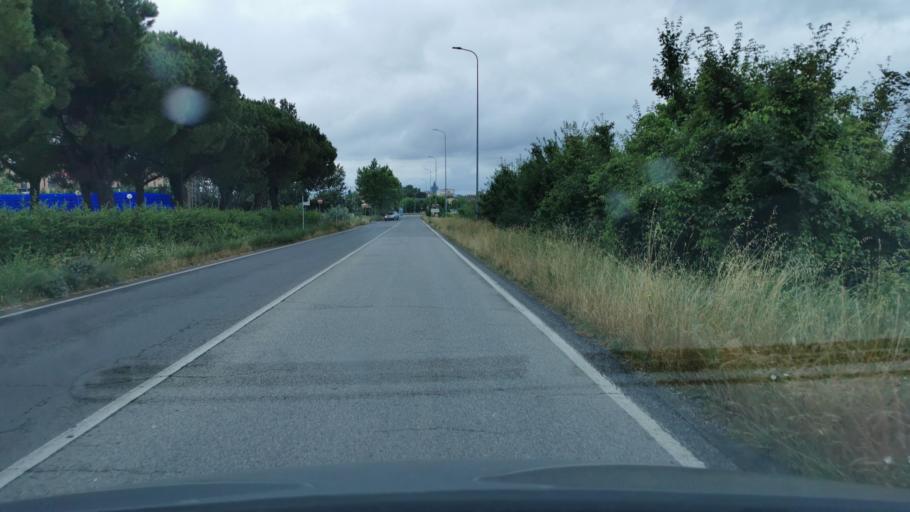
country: IT
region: Emilia-Romagna
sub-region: Provincia di Ravenna
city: Faenza
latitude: 44.3004
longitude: 11.8841
